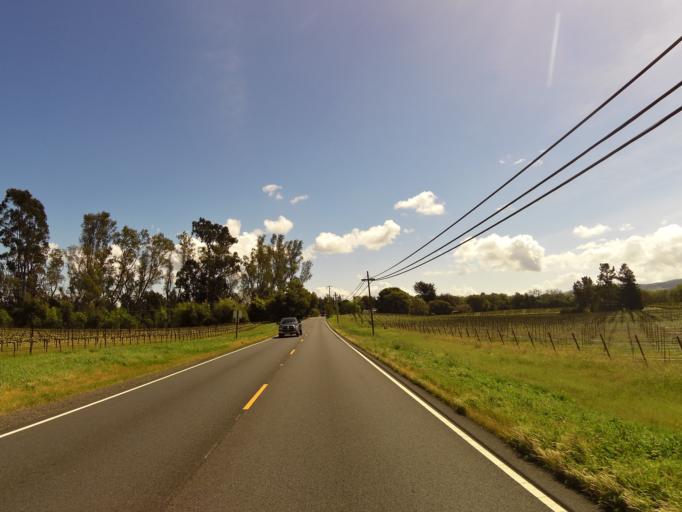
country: US
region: California
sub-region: Sonoma County
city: Sonoma
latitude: 38.2570
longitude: -122.4543
